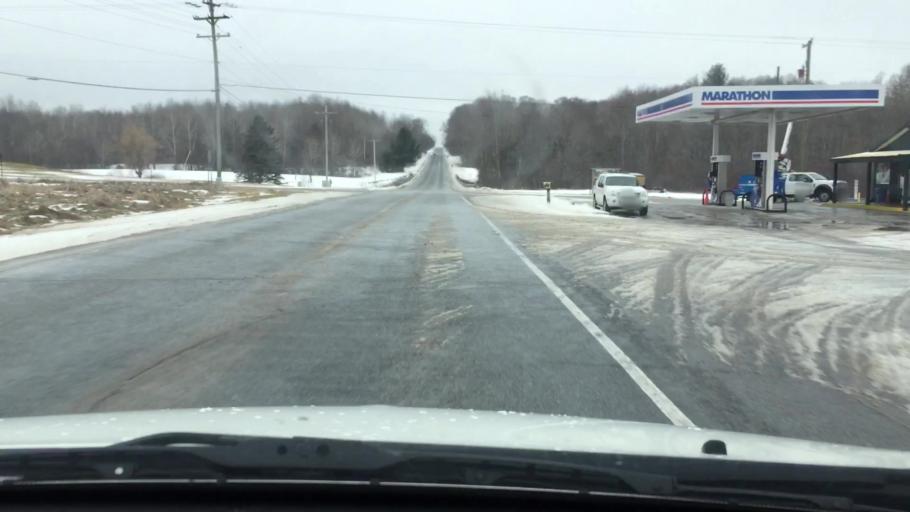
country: US
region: Michigan
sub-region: Wexford County
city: Cadillac
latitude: 44.1031
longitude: -85.4443
